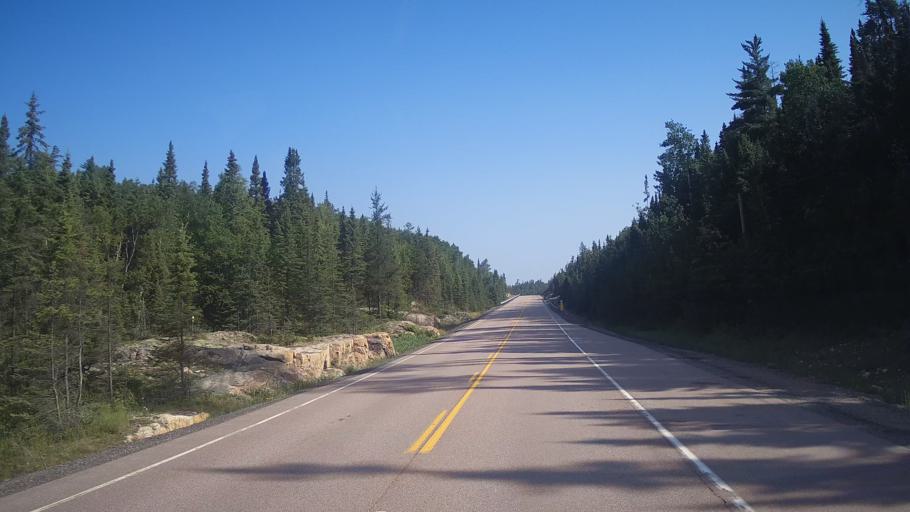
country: CA
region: Ontario
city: Rayside-Balfour
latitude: 47.0042
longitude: -81.6329
